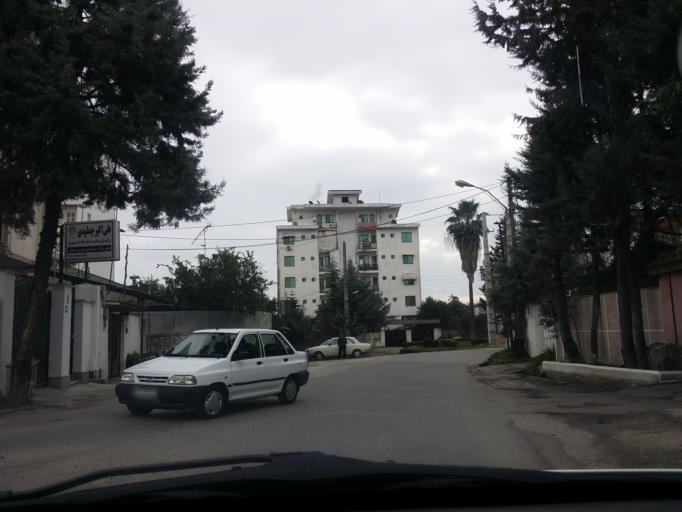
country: IR
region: Mazandaran
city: Chalus
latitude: 36.6579
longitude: 51.4210
